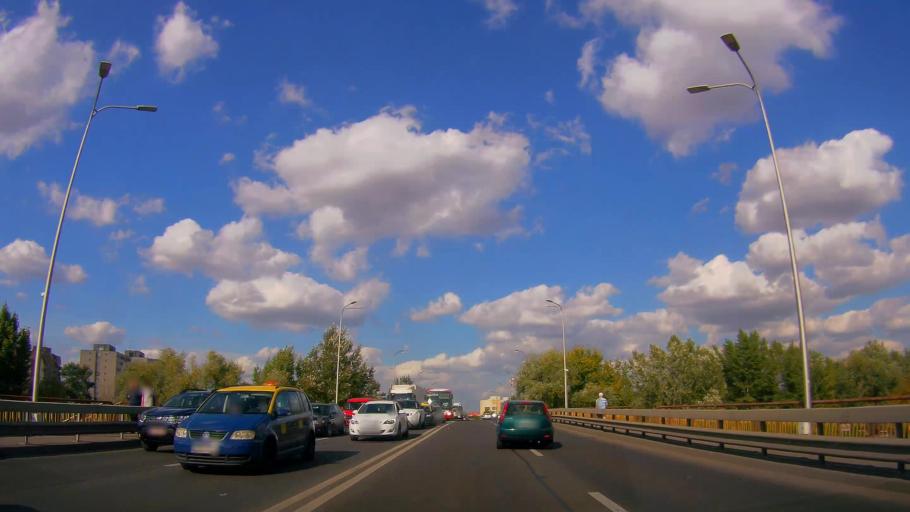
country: RO
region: Satu Mare
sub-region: Municipiul Satu Mare
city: Satu Mare
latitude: 47.7860
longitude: 22.8773
